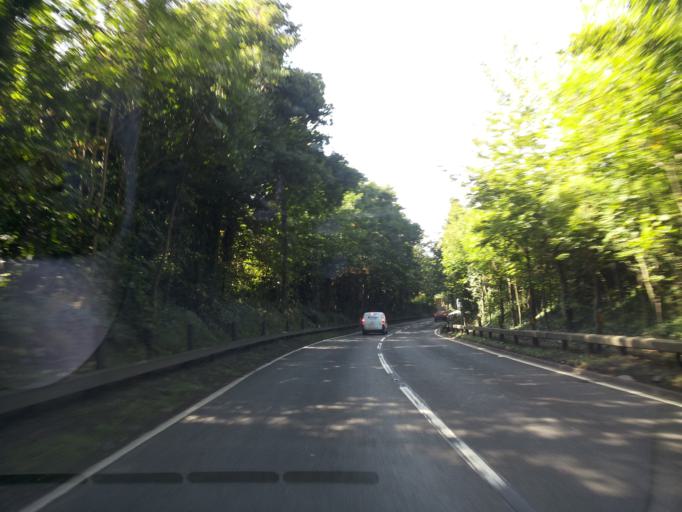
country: GB
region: England
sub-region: Kent
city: Boxley
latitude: 51.2967
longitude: 0.5740
